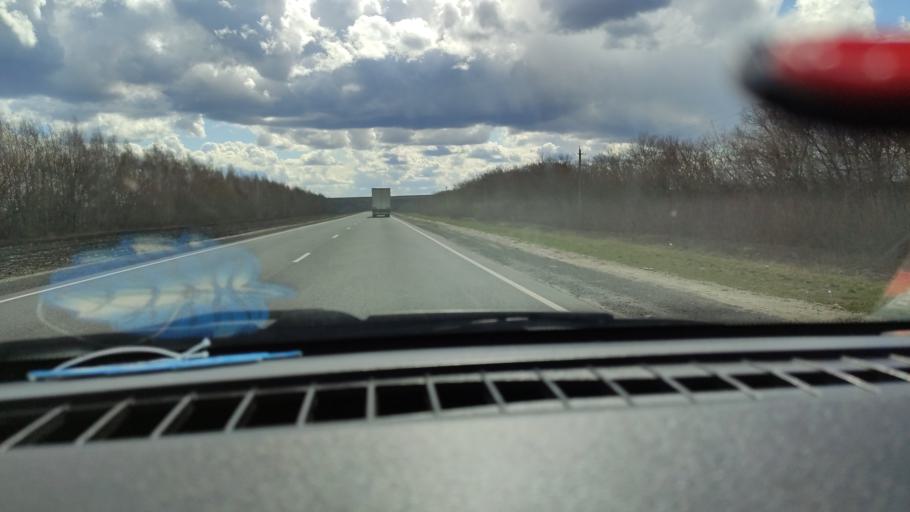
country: RU
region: Samara
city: Syzran'
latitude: 52.9803
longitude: 48.3125
